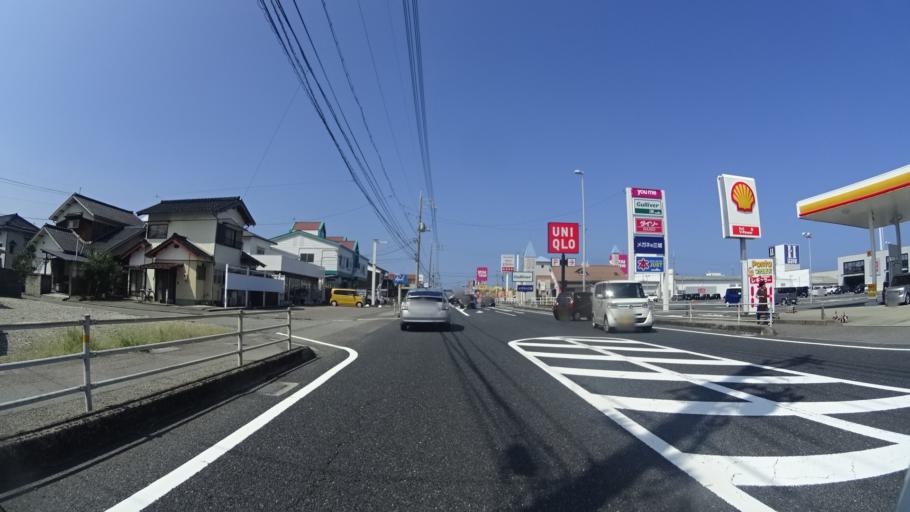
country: JP
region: Shimane
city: Masuda
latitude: 34.6895
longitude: 131.8187
